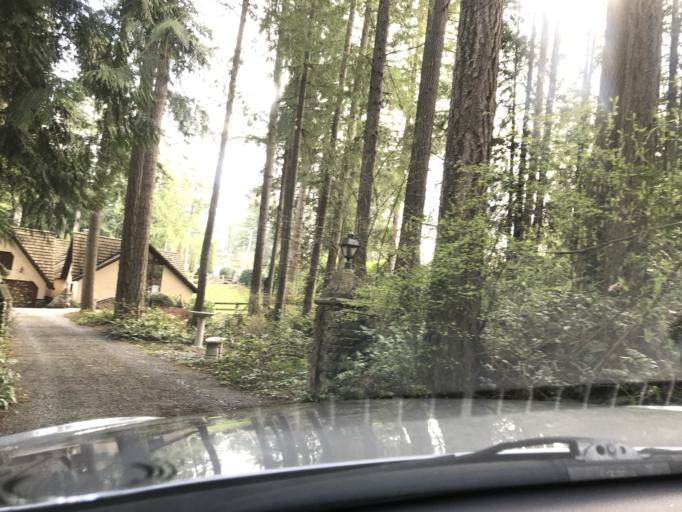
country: US
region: Washington
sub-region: King County
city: Ames Lake
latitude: 47.6368
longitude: -121.9649
